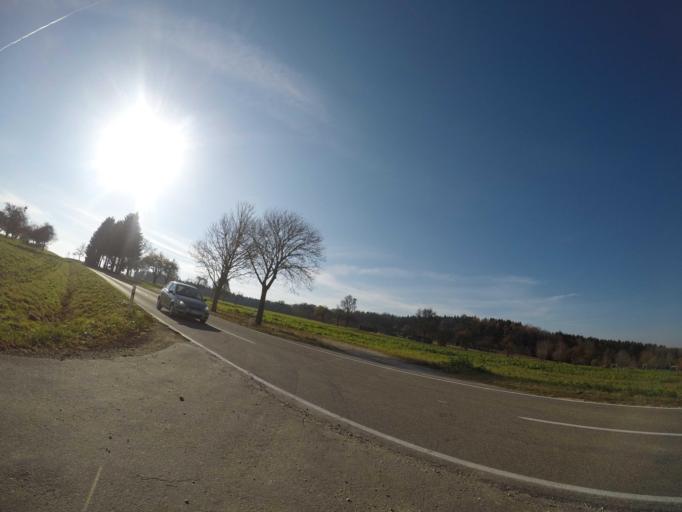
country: DE
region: Baden-Wuerttemberg
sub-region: Tuebingen Region
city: Obermarchtal
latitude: 48.2263
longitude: 9.5649
